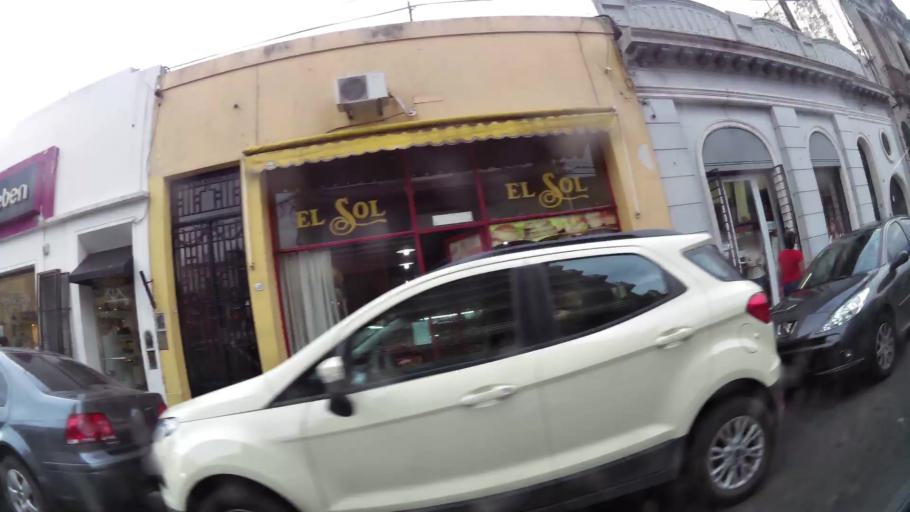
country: AR
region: Buenos Aires
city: San Nicolas de los Arroyos
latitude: -33.3336
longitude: -60.2198
